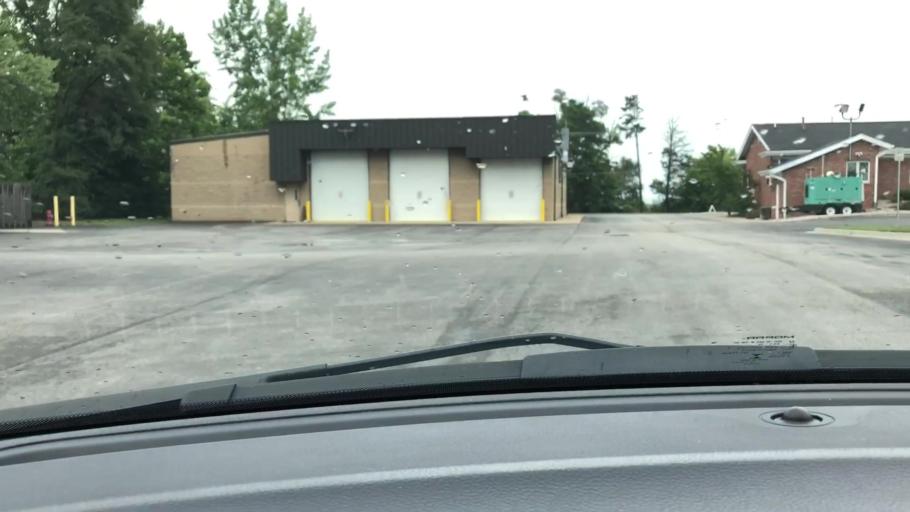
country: US
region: Michigan
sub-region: Saginaw County
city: Carrollton
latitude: 43.4902
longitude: -83.9948
